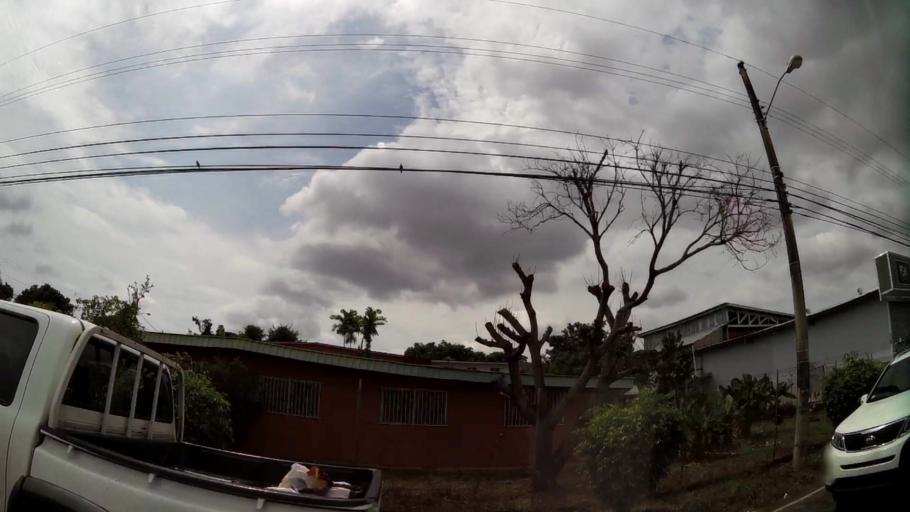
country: PA
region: Panama
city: San Miguelito
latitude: 9.0488
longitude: -79.4235
